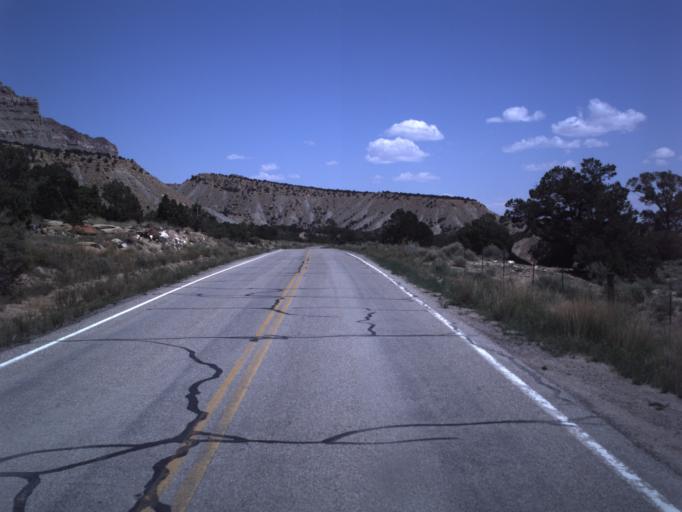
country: US
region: Utah
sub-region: Emery County
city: Orangeville
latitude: 39.2762
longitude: -111.1806
